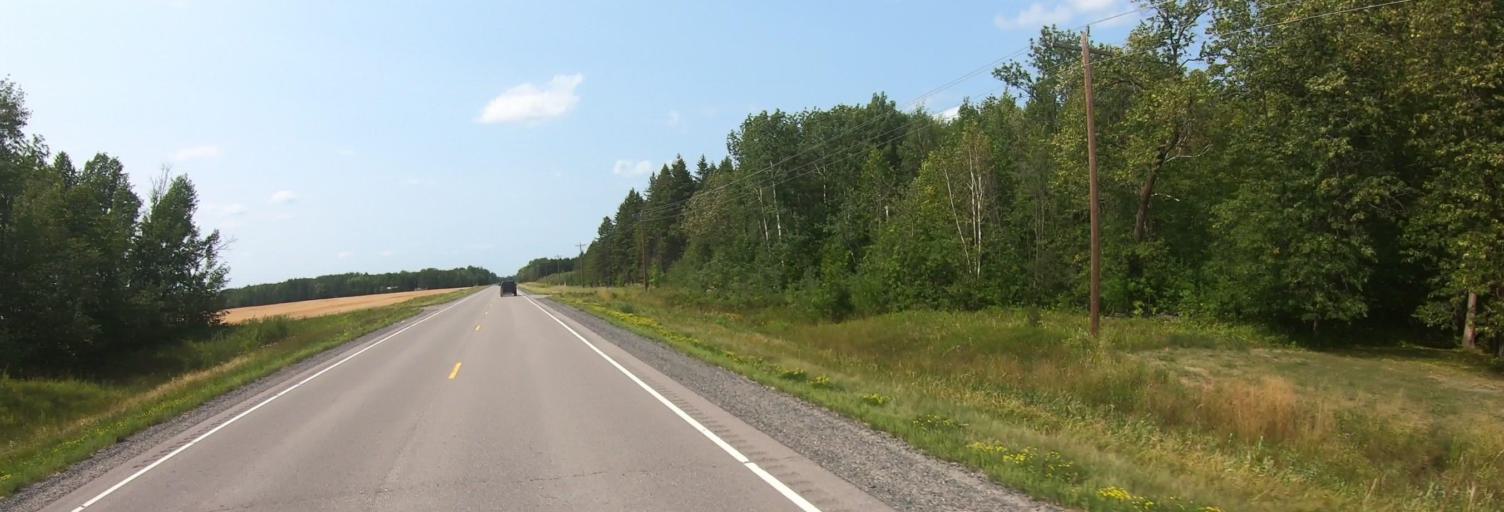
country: US
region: Minnesota
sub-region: Lake of the Woods County
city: Baudette
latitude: 48.6966
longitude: -94.5165
